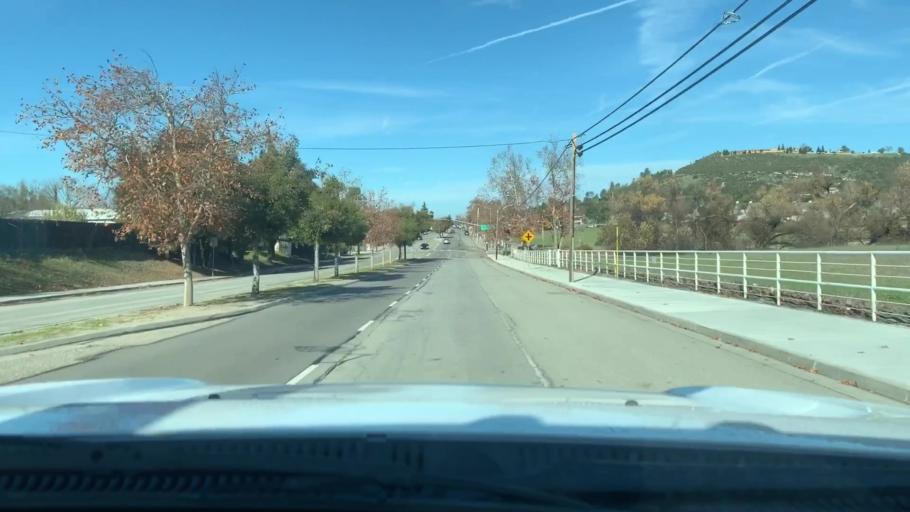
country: US
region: California
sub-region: San Luis Obispo County
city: Atascadero
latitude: 35.4589
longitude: -120.6426
